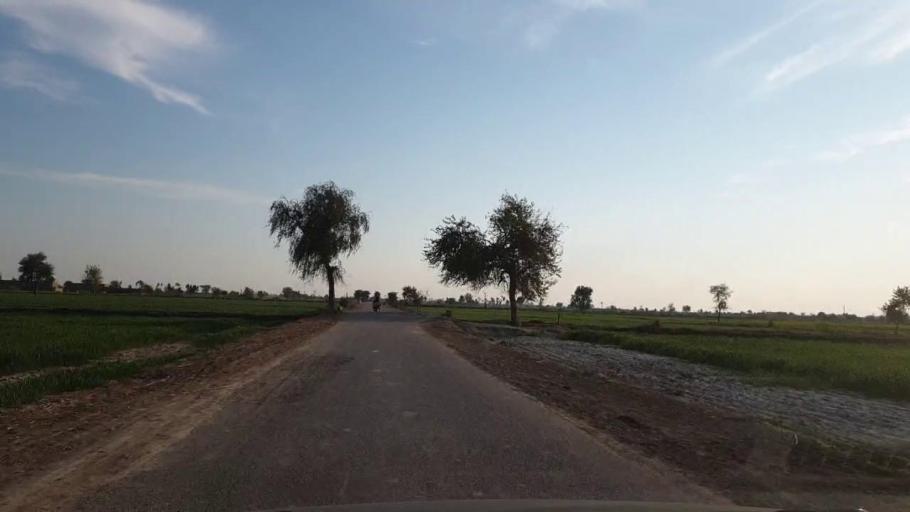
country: PK
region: Sindh
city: Khadro
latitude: 26.1671
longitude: 68.7532
